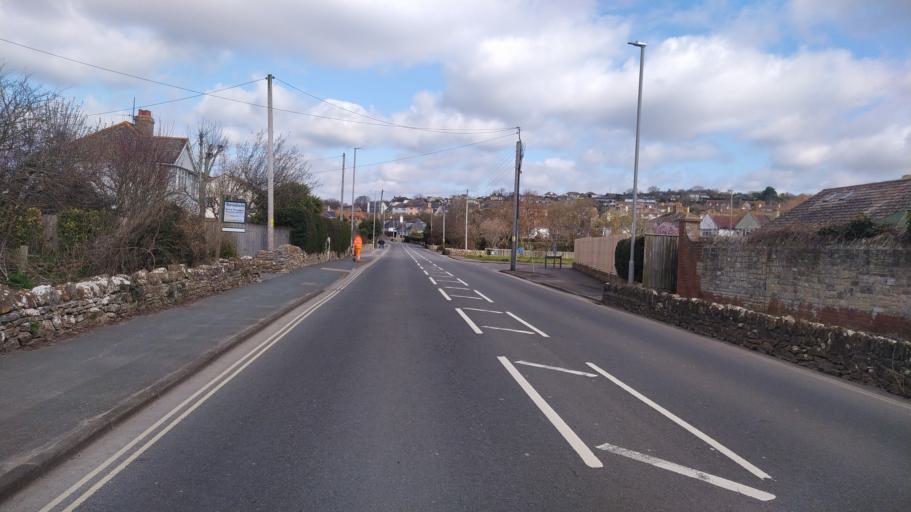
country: GB
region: England
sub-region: Dorset
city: Bridport
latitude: 50.7156
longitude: -2.7577
